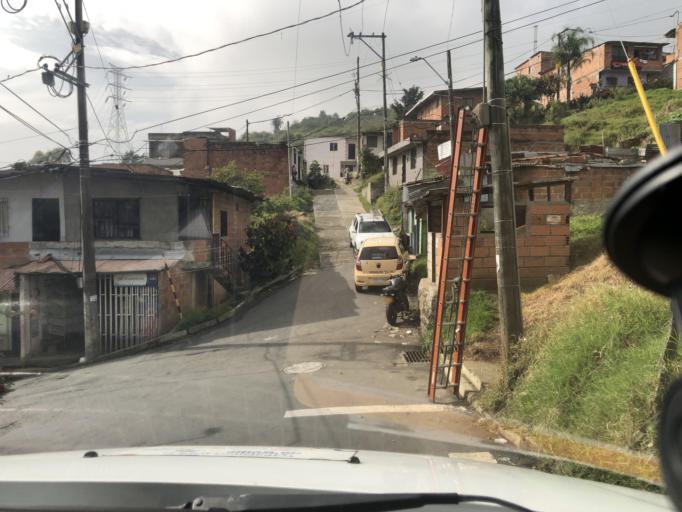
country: CO
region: Antioquia
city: Bello
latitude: 6.3148
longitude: -75.5880
